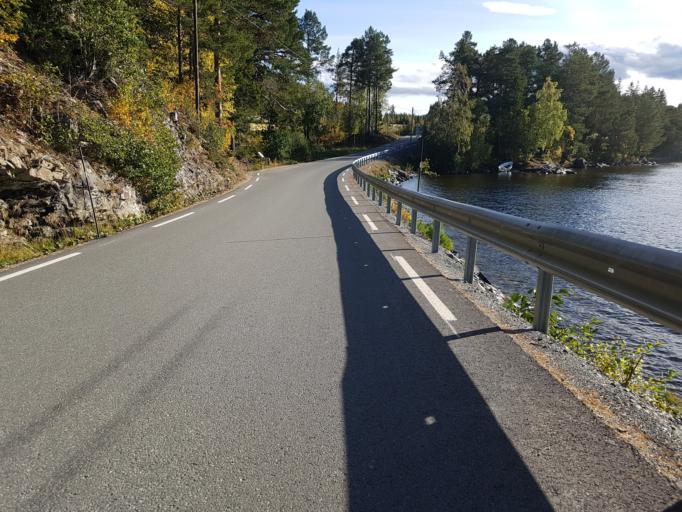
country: NO
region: Sor-Trondelag
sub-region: Malvik
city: Malvik
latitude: 63.3744
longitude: 10.6109
